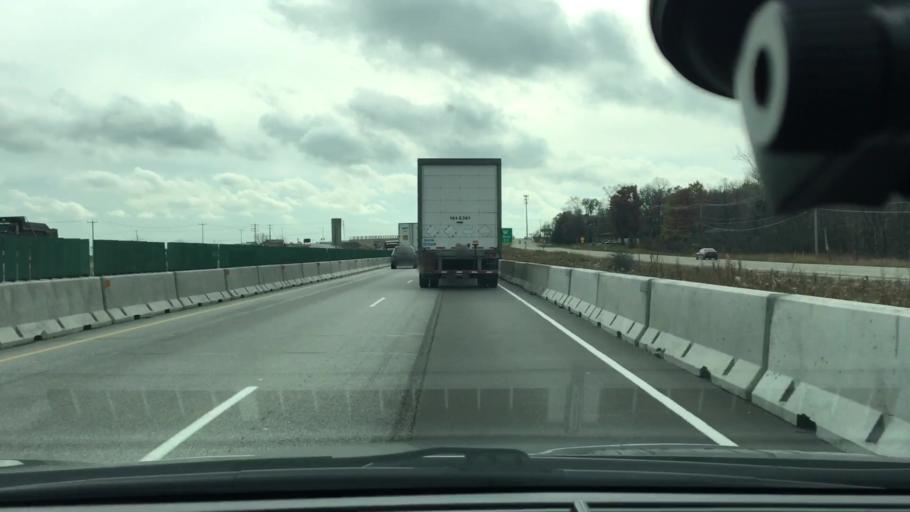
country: US
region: Wisconsin
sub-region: Racine County
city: Franksville
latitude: 42.7382
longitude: -87.9542
